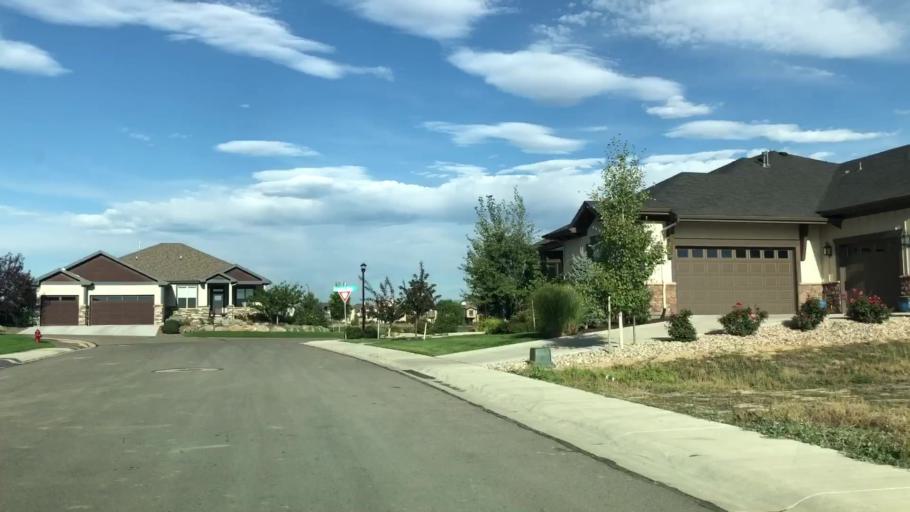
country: US
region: Colorado
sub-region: Weld County
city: Windsor
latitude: 40.4593
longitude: -104.9709
